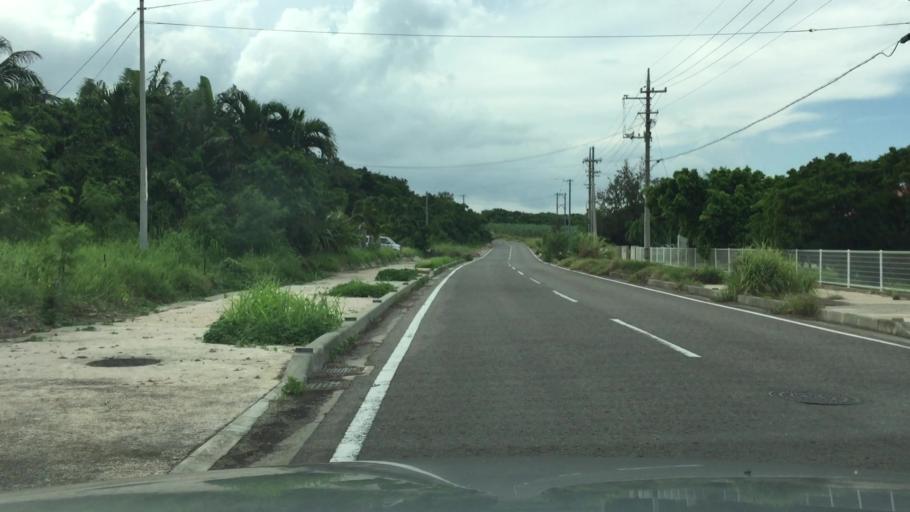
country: JP
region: Okinawa
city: Ishigaki
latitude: 24.4666
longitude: 124.1411
